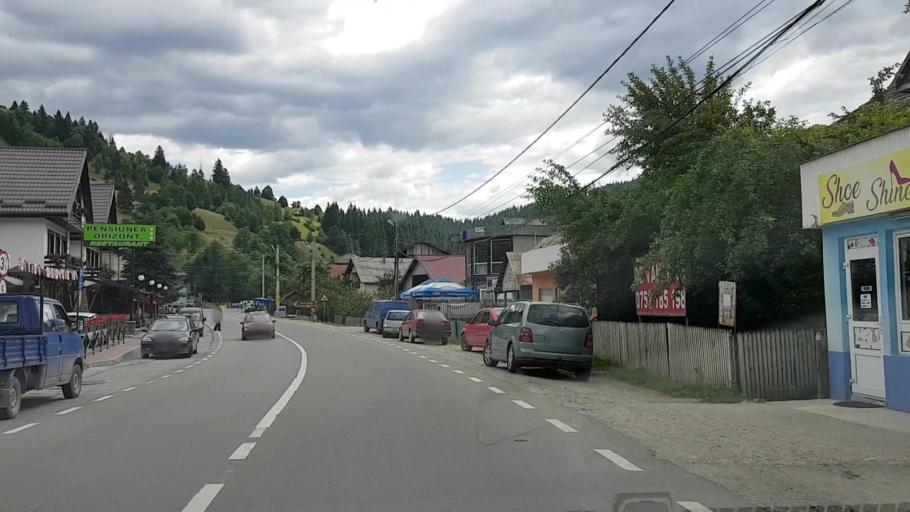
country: RO
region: Neamt
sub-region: Comuna Farcasa
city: Farcasa
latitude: 47.1567
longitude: 25.8375
